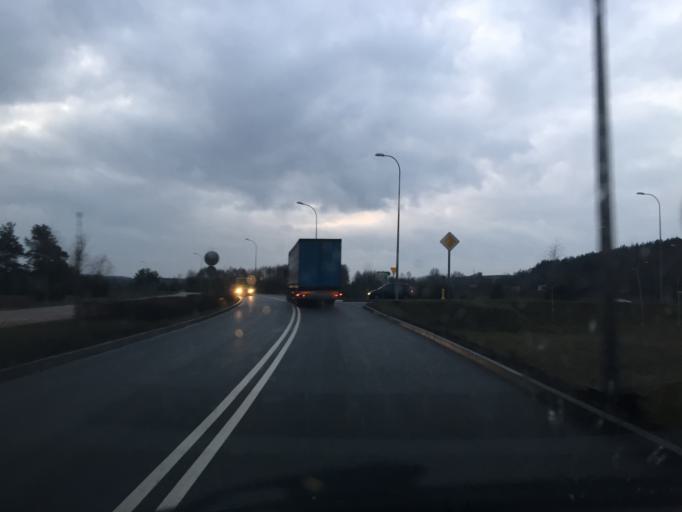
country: PL
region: Kujawsko-Pomorskie
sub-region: Powiat brodnicki
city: Brodnica
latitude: 53.2488
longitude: 19.3737
